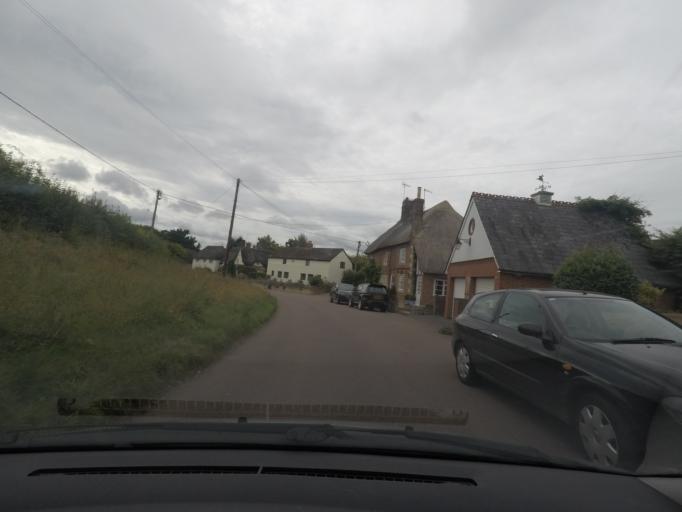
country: GB
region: England
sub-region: Wiltshire
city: Woodborough
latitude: 51.3308
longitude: -1.8038
